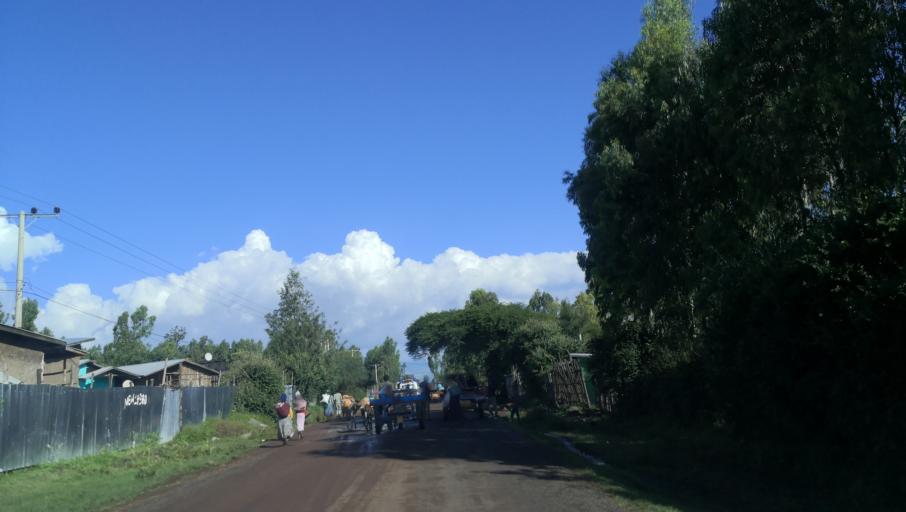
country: ET
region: Oromiya
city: Tulu Bolo
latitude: 8.6445
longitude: 38.2217
